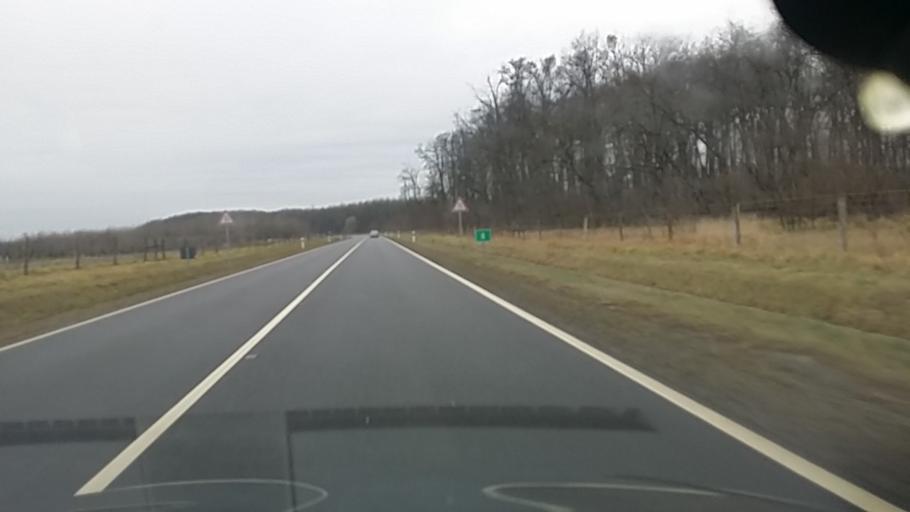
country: HU
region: Hajdu-Bihar
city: Debrecen
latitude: 47.6036
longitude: 21.6248
